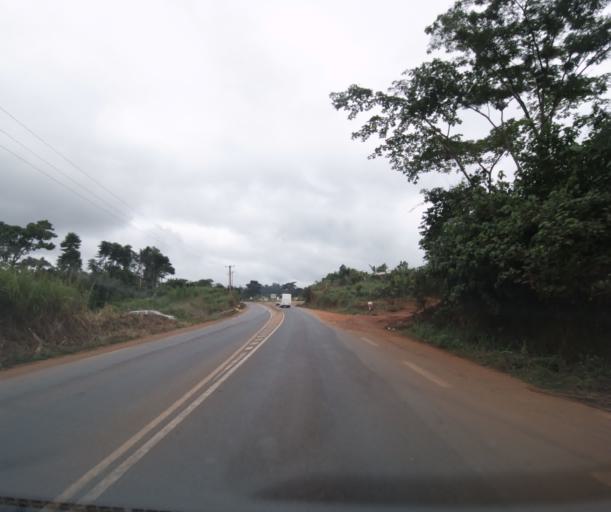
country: CM
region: Centre
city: Mbankomo
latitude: 3.7888
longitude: 11.4439
